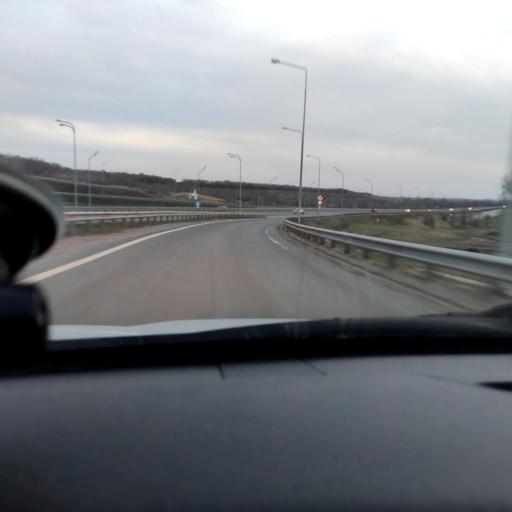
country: RU
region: Samara
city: Smyshlyayevka
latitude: 53.1495
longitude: 50.3816
